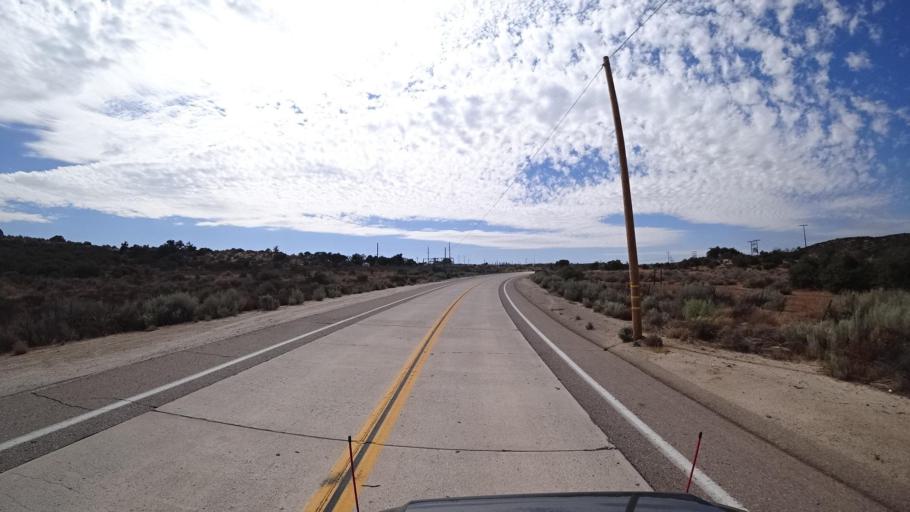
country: MX
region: Baja California
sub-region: Tecate
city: Cereso del Hongo
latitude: 32.6628
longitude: -116.2691
